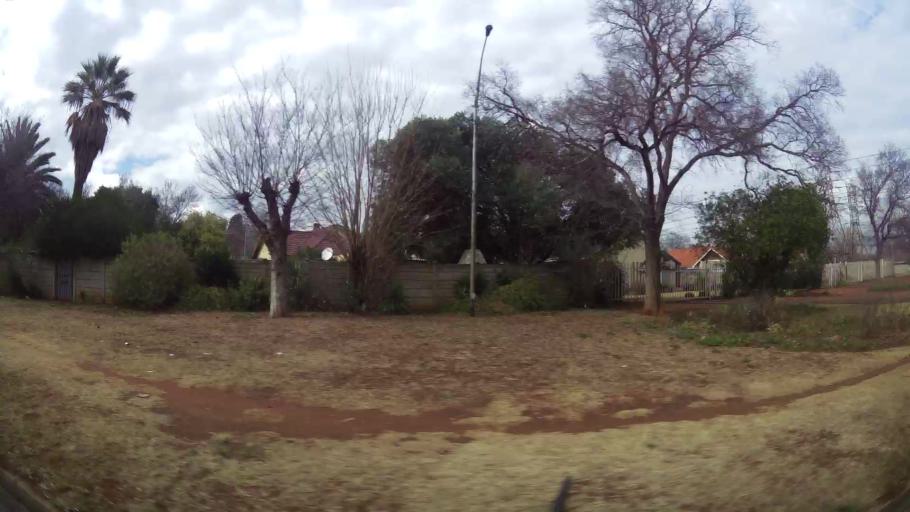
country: ZA
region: Gauteng
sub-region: Sedibeng District Municipality
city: Vereeniging
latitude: -26.6448
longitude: 27.9707
